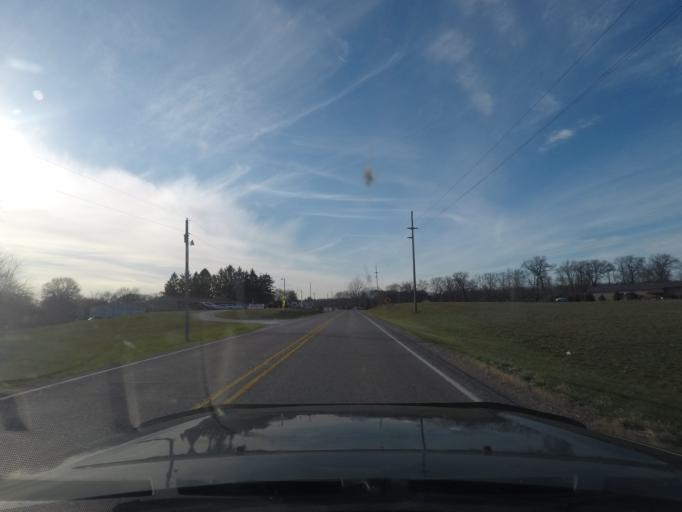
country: US
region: Indiana
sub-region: Saint Joseph County
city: Walkerton
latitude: 41.4494
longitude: -86.4418
